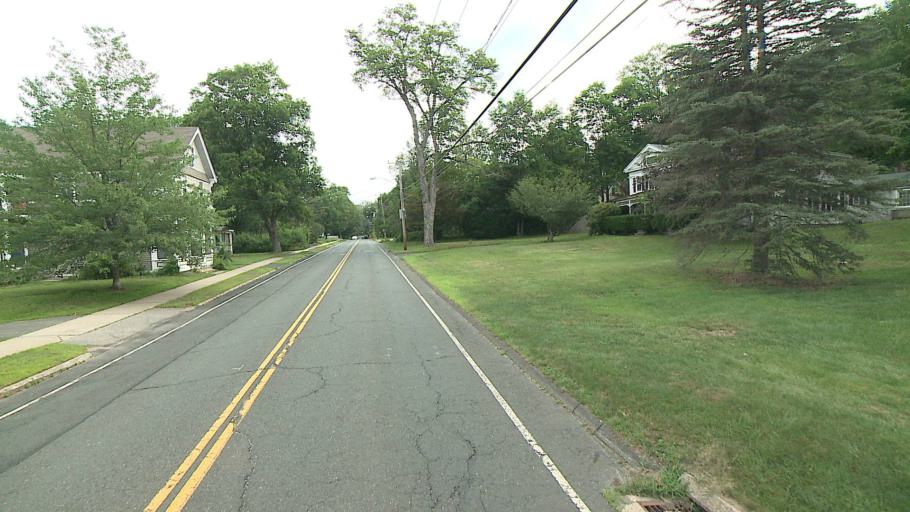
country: US
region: Connecticut
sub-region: Hartford County
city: Collinsville
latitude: 41.8150
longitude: -72.9188
